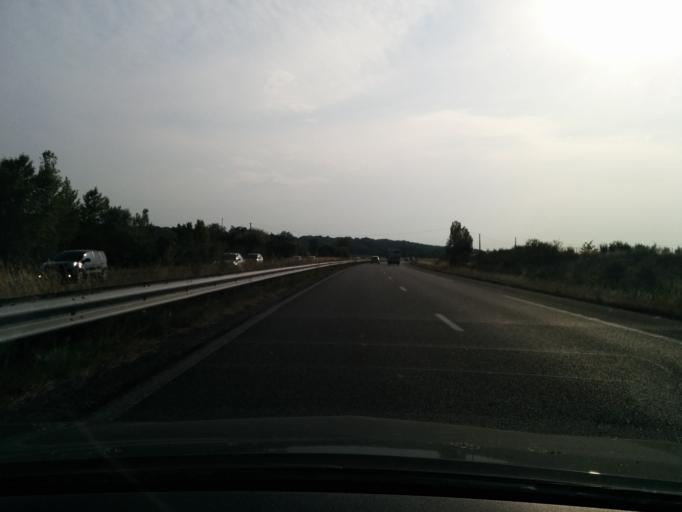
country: FR
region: Midi-Pyrenees
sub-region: Departement du Tarn
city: Saint-Sulpice-la-Pointe
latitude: 43.7538
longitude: 1.6994
